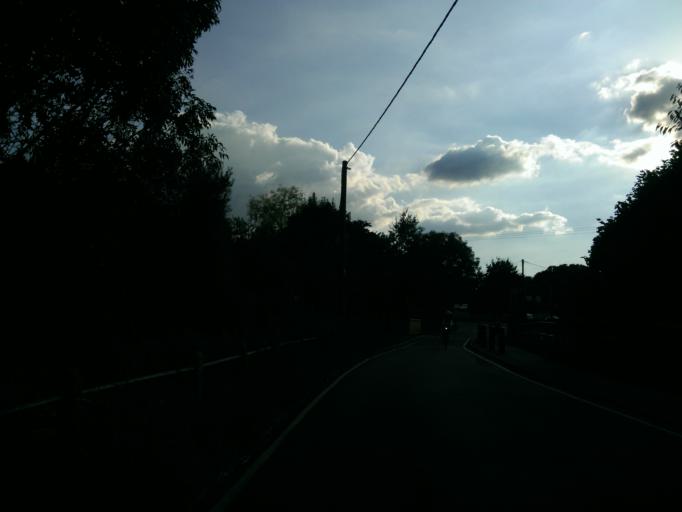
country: GB
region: England
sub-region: Essex
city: Sible Hedingham
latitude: 51.9904
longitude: 0.5870
